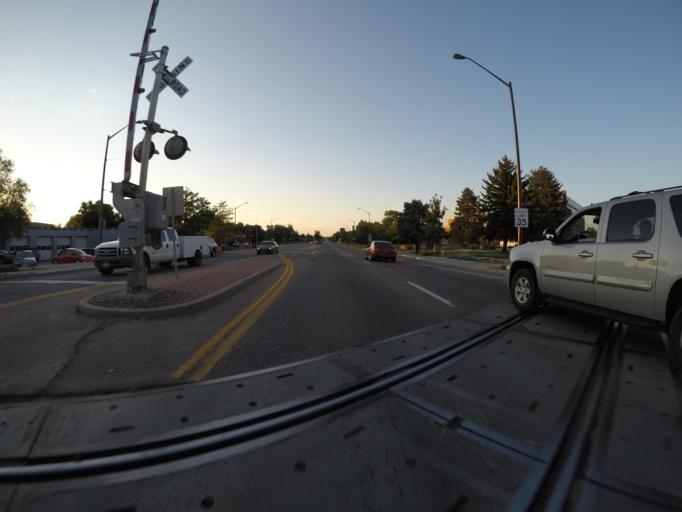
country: US
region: Colorado
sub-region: Larimer County
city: Fort Collins
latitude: 40.5932
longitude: -105.0767
